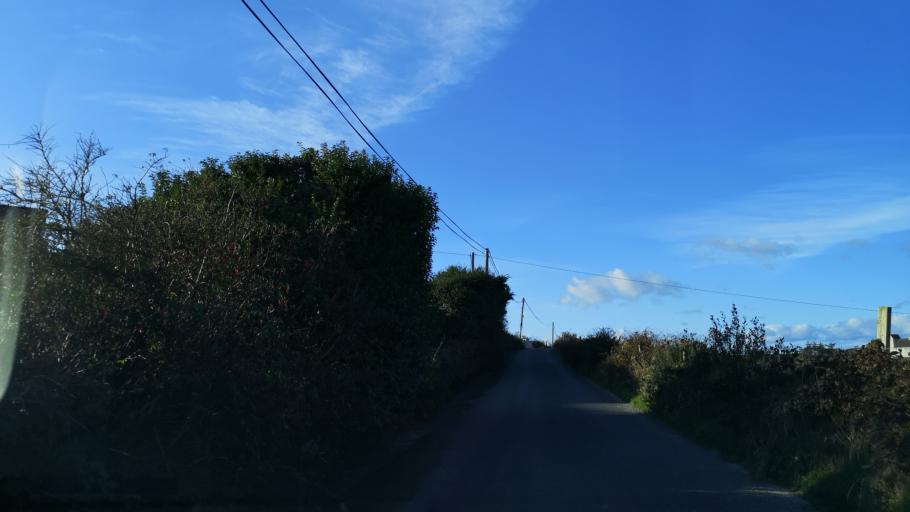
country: IE
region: Connaught
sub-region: County Galway
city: Clifden
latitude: 53.5074
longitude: -10.0894
